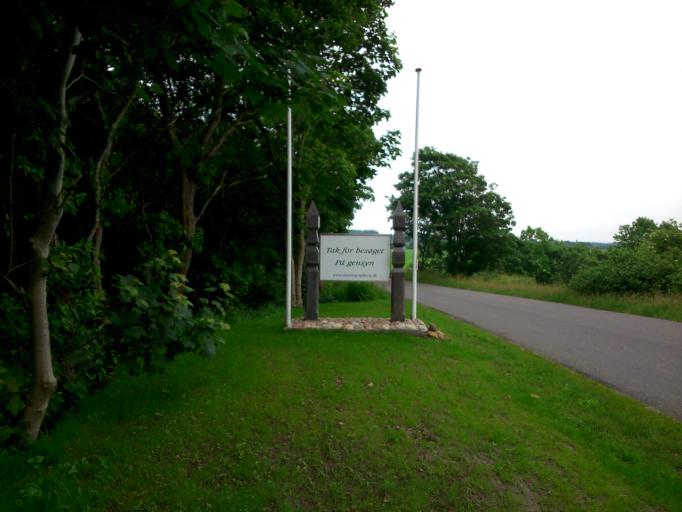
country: DK
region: Central Jutland
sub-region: Ringkobing-Skjern Kommune
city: Skjern
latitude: 55.9991
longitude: 8.4212
